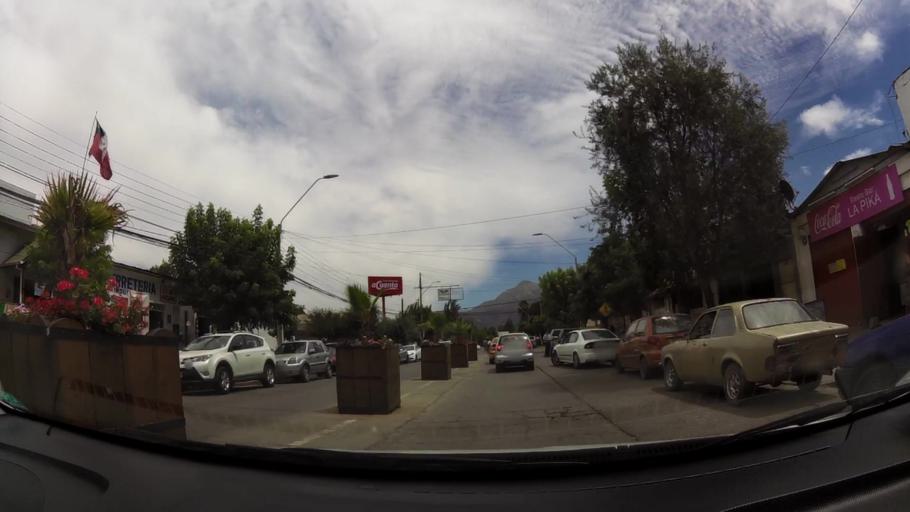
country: CL
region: O'Higgins
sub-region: Provincia de Cachapoal
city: Graneros
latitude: -34.0673
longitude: -70.7290
